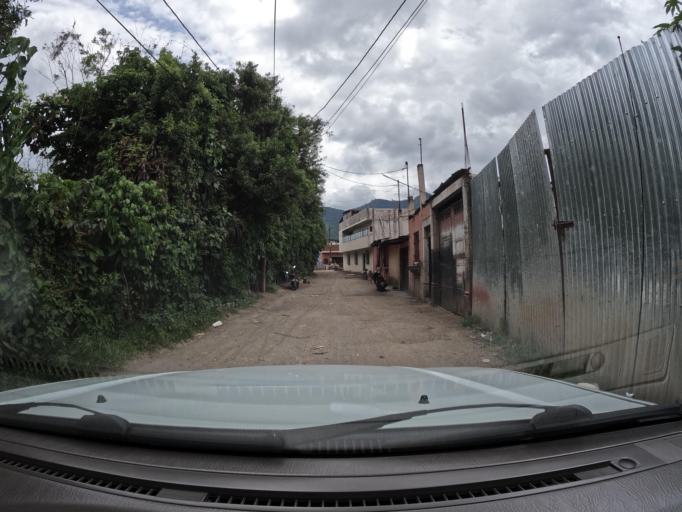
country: GT
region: Sacatepequez
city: Jocotenango
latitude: 14.5726
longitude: -90.7392
